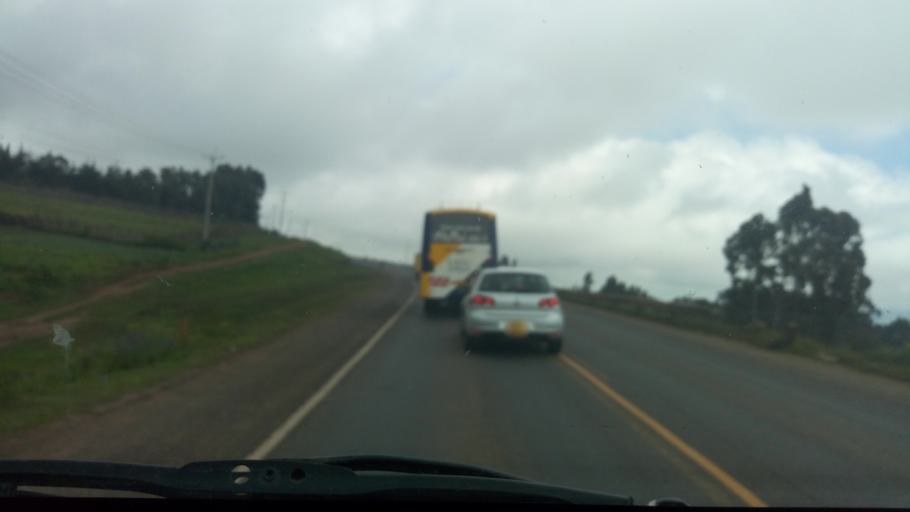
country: KE
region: Nakuru
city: Kijabe
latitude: -0.8464
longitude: 36.5483
